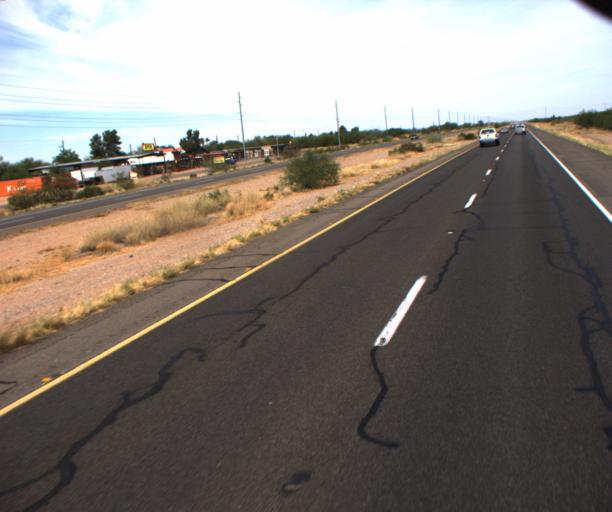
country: US
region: Arizona
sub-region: Maricopa County
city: Sun City West
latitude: 33.7077
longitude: -112.4385
